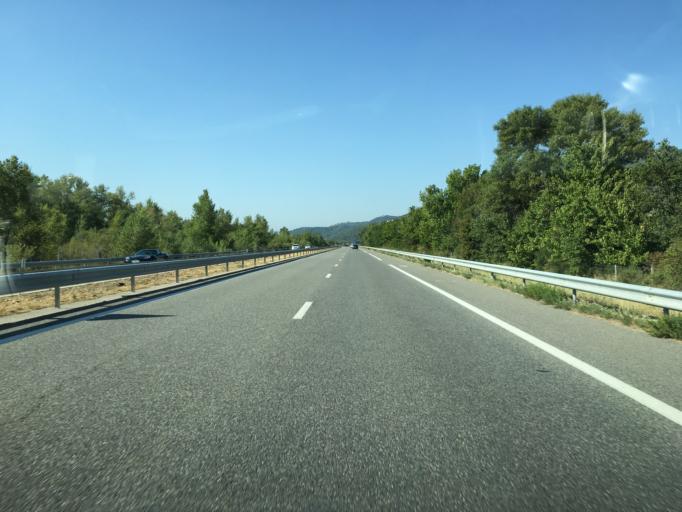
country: FR
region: Provence-Alpes-Cote d'Azur
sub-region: Departement des Alpes-de-Haute-Provence
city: Peyruis
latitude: 44.0144
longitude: 5.9389
